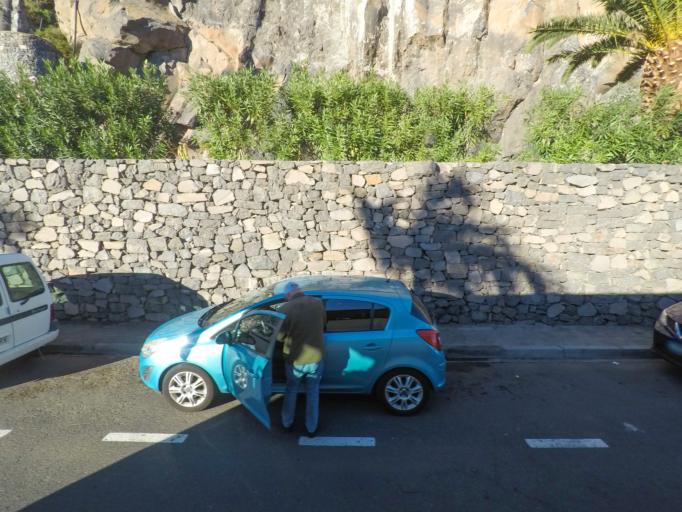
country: ES
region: Canary Islands
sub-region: Provincia de Santa Cruz de Tenerife
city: San Sebastian de la Gomera
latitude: 28.0899
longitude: -17.1087
